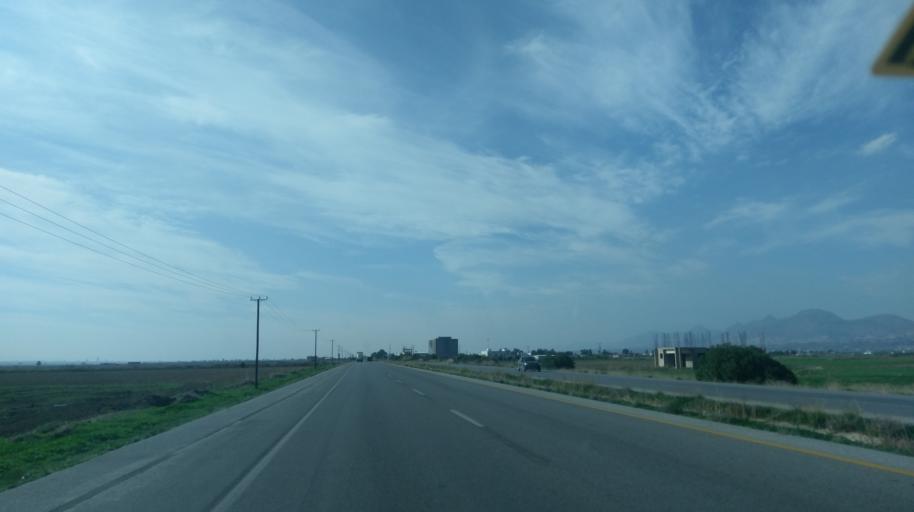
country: CY
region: Larnaka
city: Athienou
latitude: 35.2112
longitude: 33.5422
